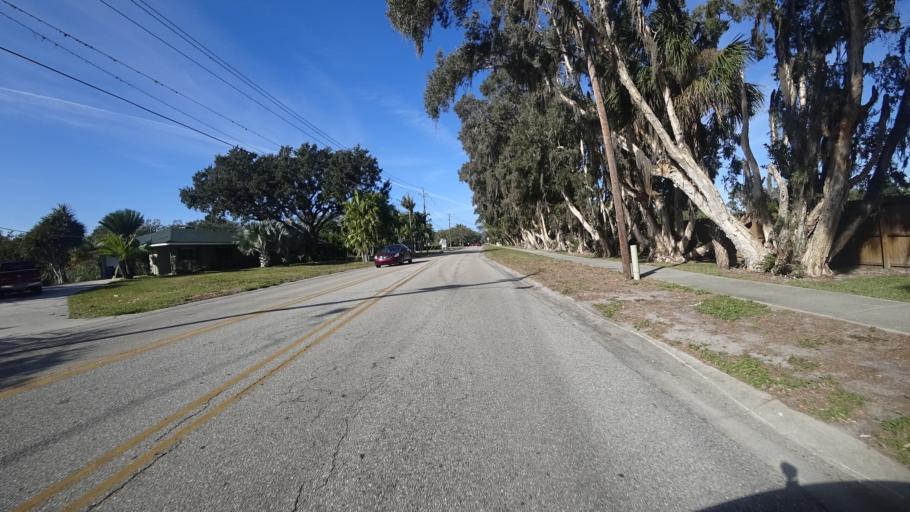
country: US
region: Florida
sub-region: Manatee County
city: West Bradenton
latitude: 27.4813
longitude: -82.6151
